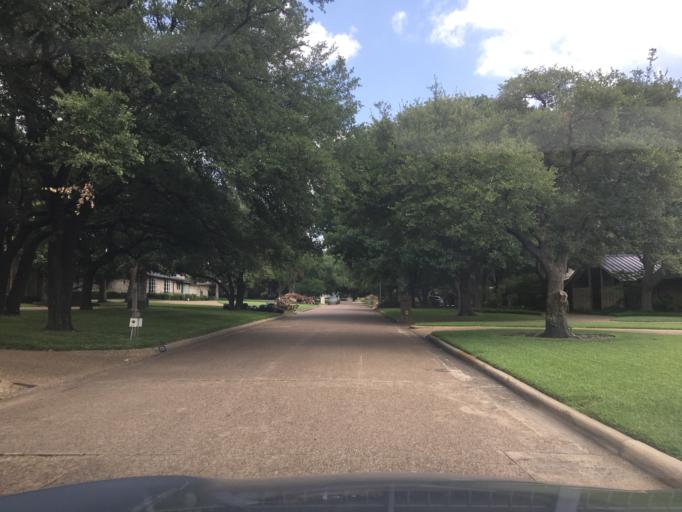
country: US
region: Texas
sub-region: Dallas County
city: University Park
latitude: 32.8971
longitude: -96.8181
